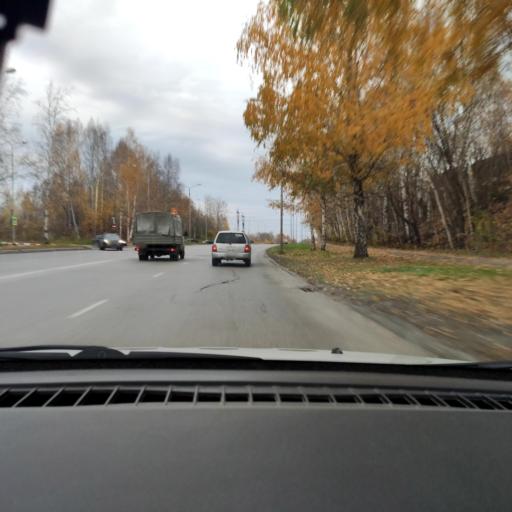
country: RU
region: Perm
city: Perm
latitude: 58.0978
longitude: 56.3858
